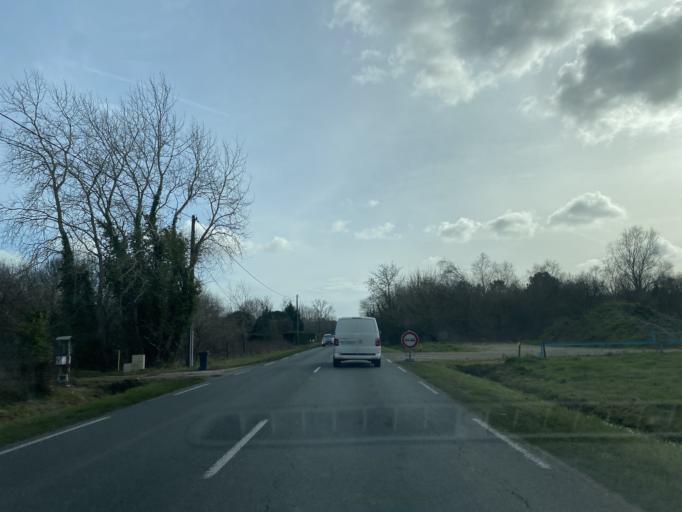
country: FR
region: Aquitaine
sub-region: Departement de la Gironde
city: Le Taillan-Medoc
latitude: 44.9259
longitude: -0.6772
